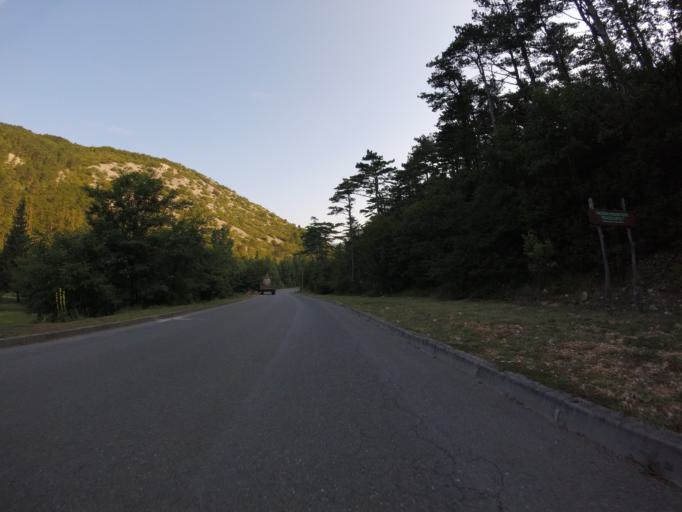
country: HR
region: Primorsko-Goranska
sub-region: Grad Crikvenica
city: Crikvenica
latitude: 45.1871
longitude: 14.7004
